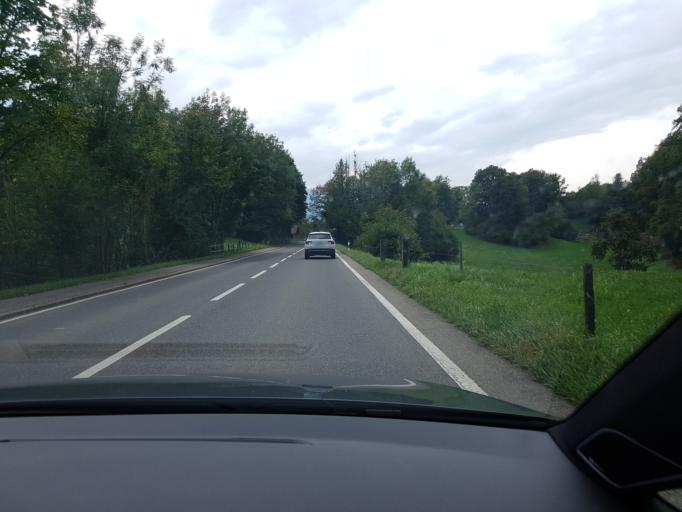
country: CH
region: Bern
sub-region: Interlaken-Oberhasli District
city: Ringgenberg
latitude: 46.7102
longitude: 7.9153
